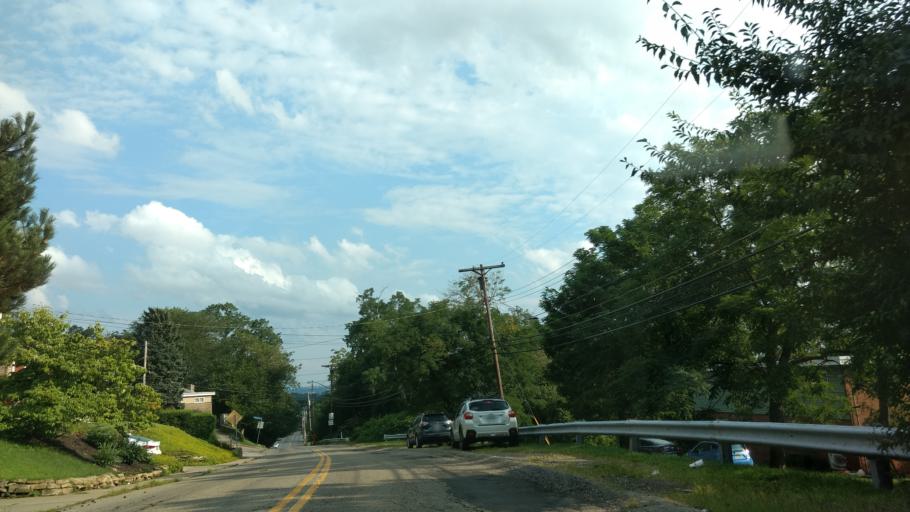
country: US
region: Pennsylvania
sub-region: Allegheny County
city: Bellevue
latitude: 40.4906
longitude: -80.0353
